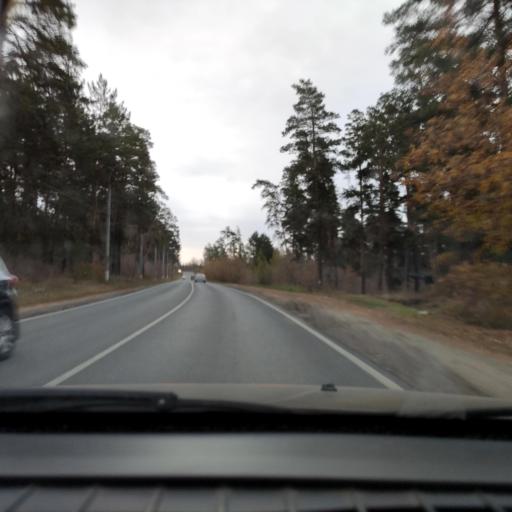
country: RU
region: Samara
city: Tol'yatti
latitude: 53.4735
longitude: 49.3806
